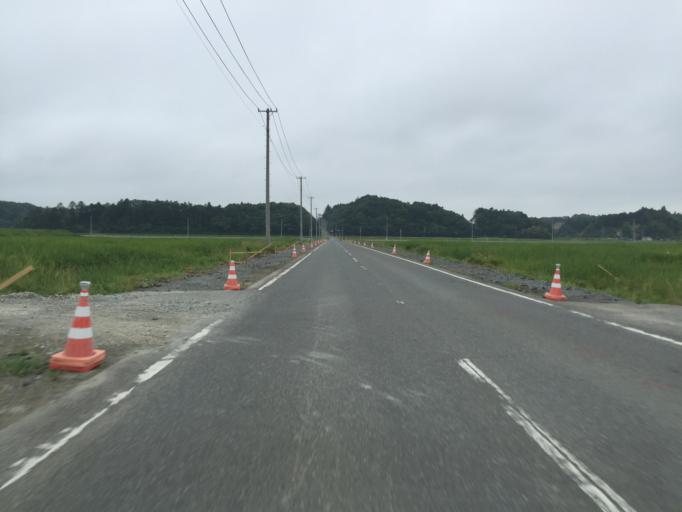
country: JP
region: Fukushima
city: Namie
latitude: 37.6823
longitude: 141.0044
